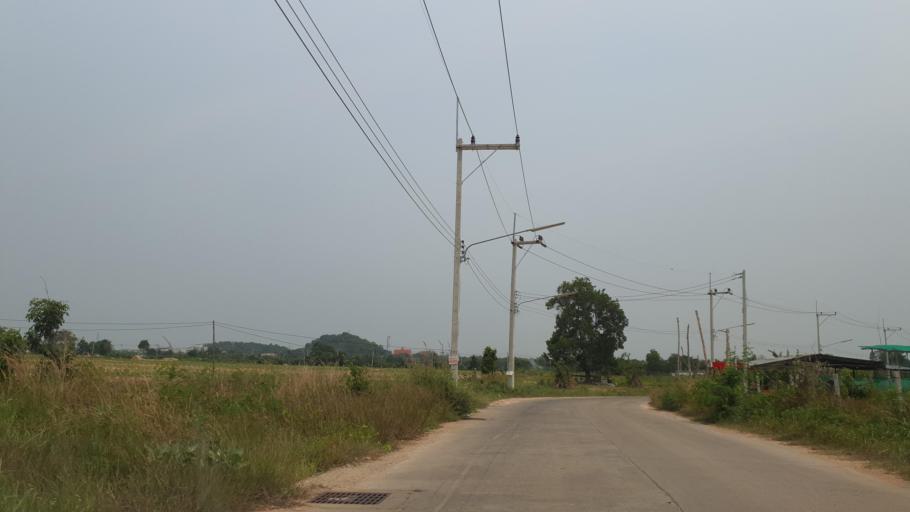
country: TH
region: Chon Buri
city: Phatthaya
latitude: 12.8907
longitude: 100.9271
